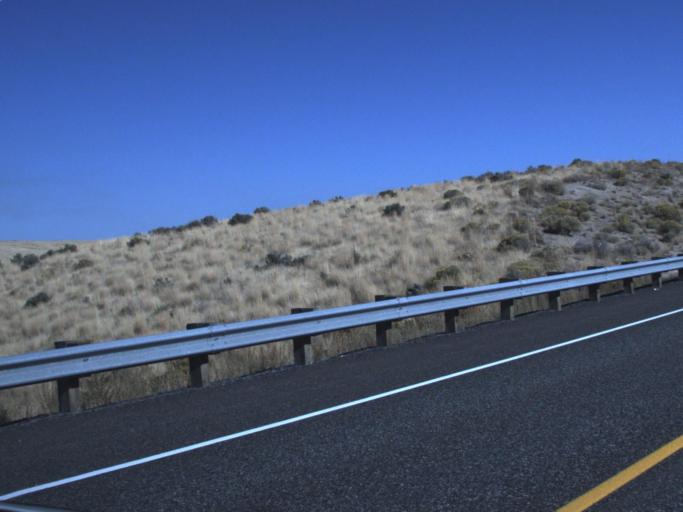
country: US
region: Washington
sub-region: Benton County
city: Highland
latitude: 46.1403
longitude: -119.1052
